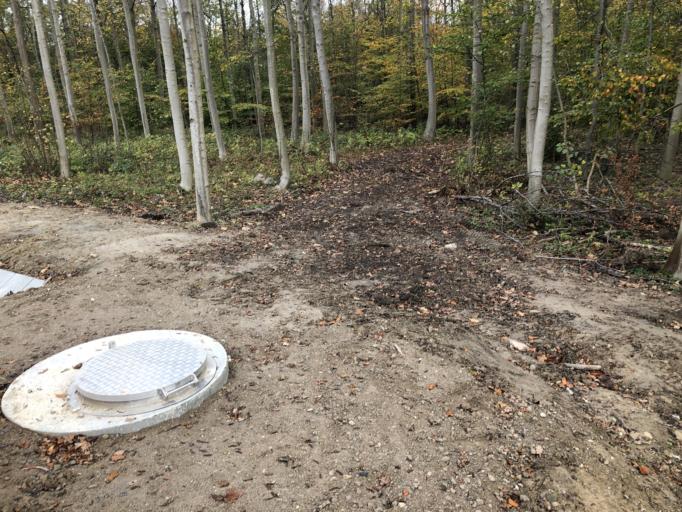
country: DK
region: Zealand
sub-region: Guldborgsund Kommune
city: Norre Alslev
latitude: 54.9226
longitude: 11.8775
